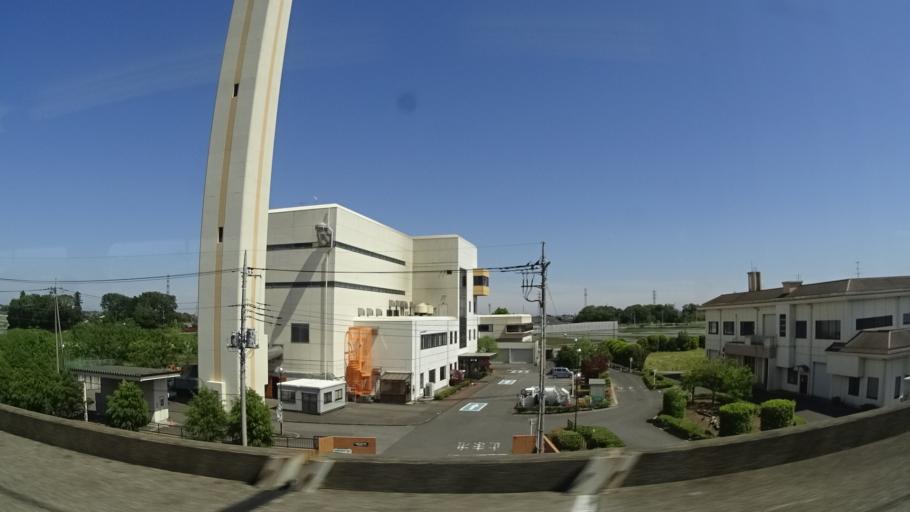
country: JP
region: Saitama
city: Kurihashi
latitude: 36.0983
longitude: 139.6984
